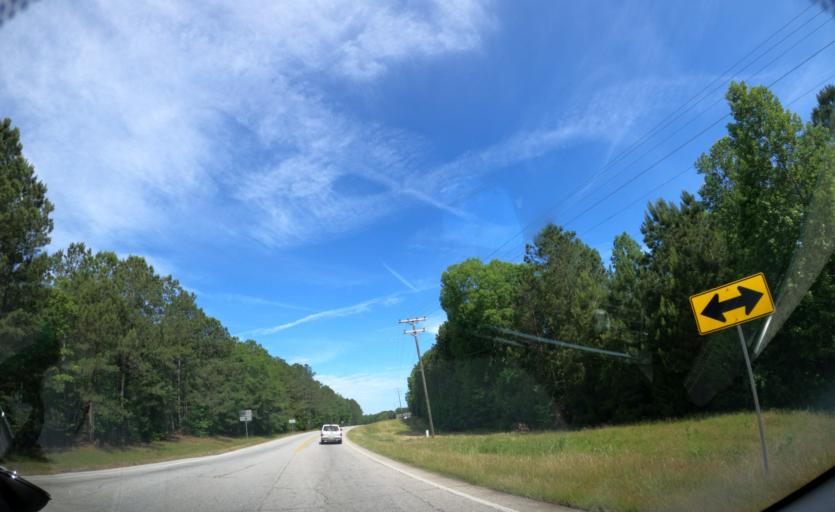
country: US
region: South Carolina
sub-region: Abbeville County
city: Calhoun Falls
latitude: 34.0599
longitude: -82.7158
